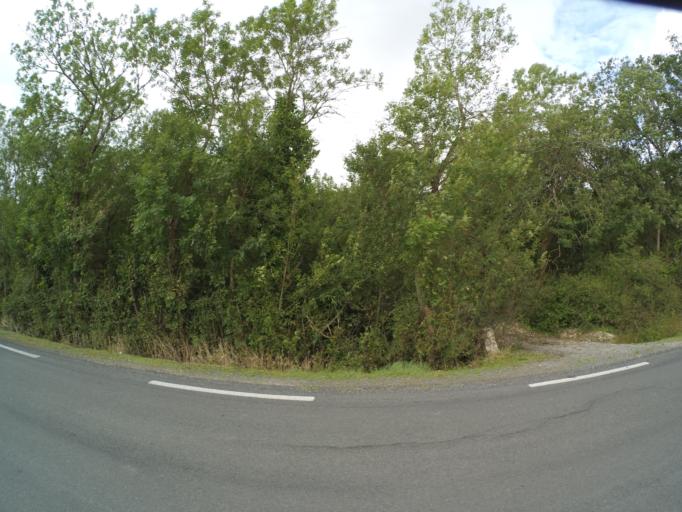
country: FR
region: Aquitaine
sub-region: Departement de la Gironde
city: Macau
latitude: 45.0023
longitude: -0.6025
